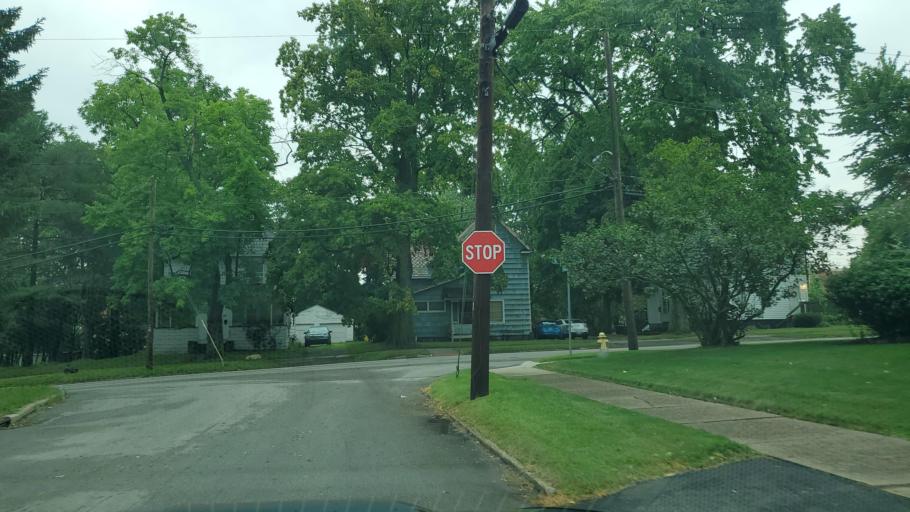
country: US
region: Ohio
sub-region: Trumbull County
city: Warren
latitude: 41.2409
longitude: -80.8057
